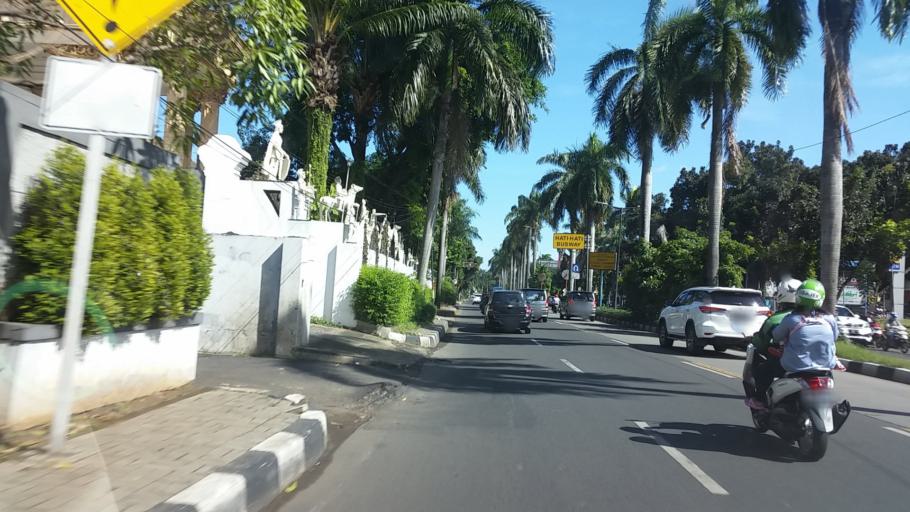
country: ID
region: Banten
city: South Tangerang
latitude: -6.2859
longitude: 106.7802
